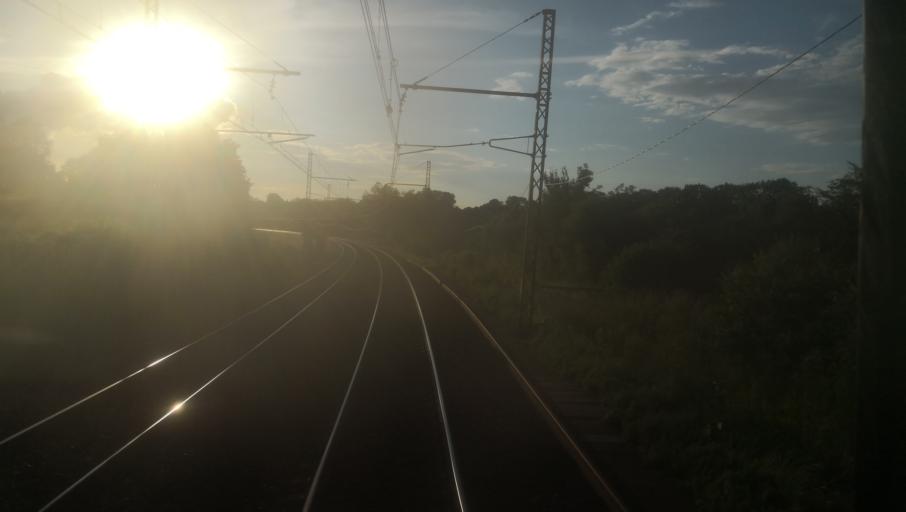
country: FR
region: Centre
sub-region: Departement de l'Indre
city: Le Pechereau
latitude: 46.4930
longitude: 1.5340
